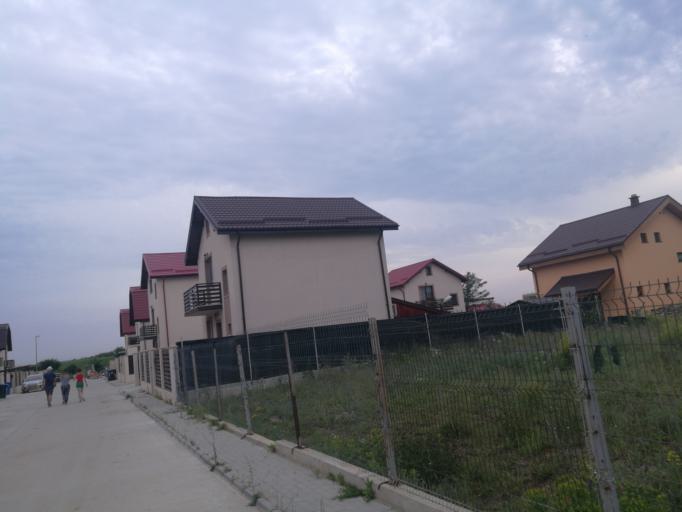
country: RO
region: Ilfov
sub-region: Comuna Vidra
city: Vidra
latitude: 44.2764
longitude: 26.1839
